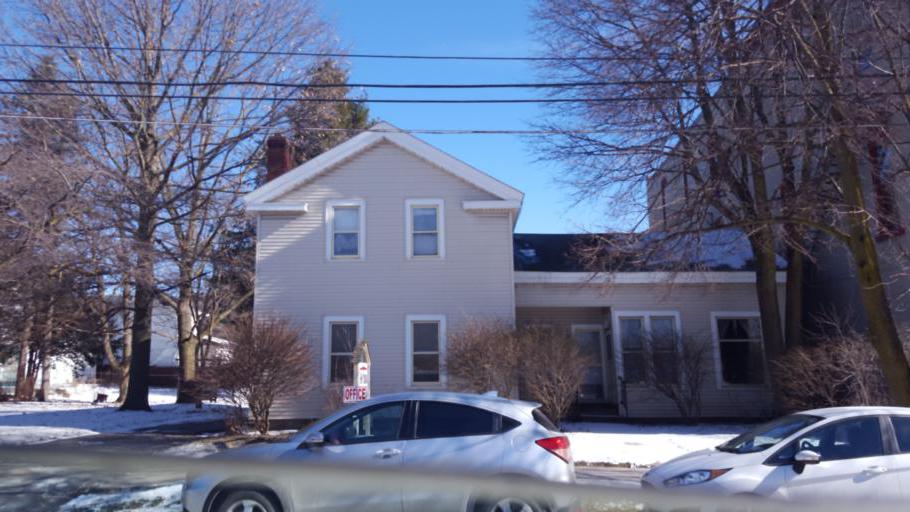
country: US
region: New York
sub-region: Allegany County
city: Wellsville
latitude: 42.1231
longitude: -77.9501
